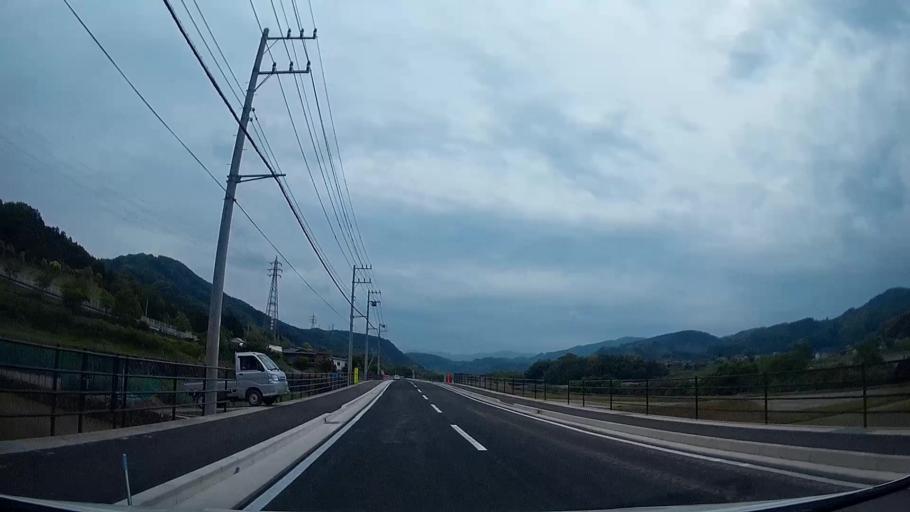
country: JP
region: Shizuoka
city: Ito
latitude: 34.9562
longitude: 138.9438
